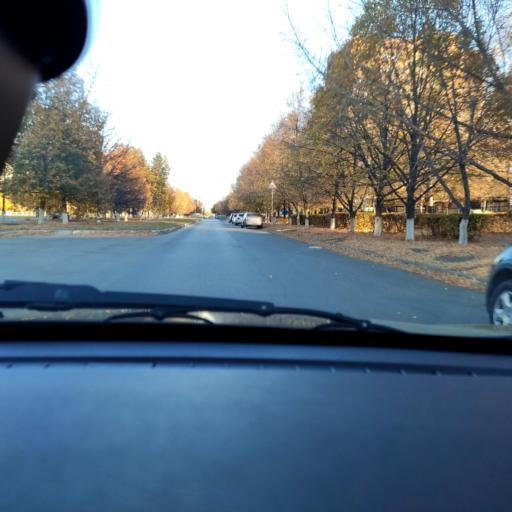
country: RU
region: Samara
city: Tol'yatti
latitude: 53.5255
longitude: 49.3162
